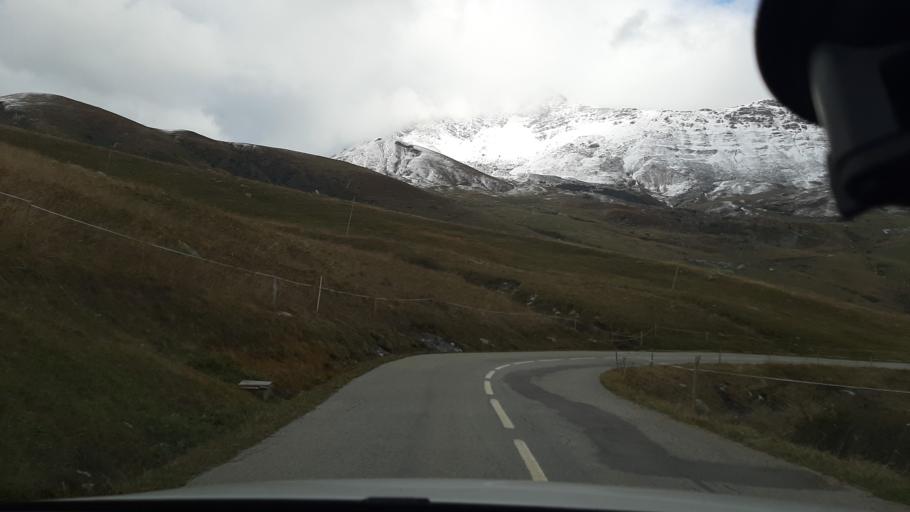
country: FR
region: Rhone-Alpes
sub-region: Departement de la Savoie
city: La Chambre
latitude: 45.4276
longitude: 6.3681
